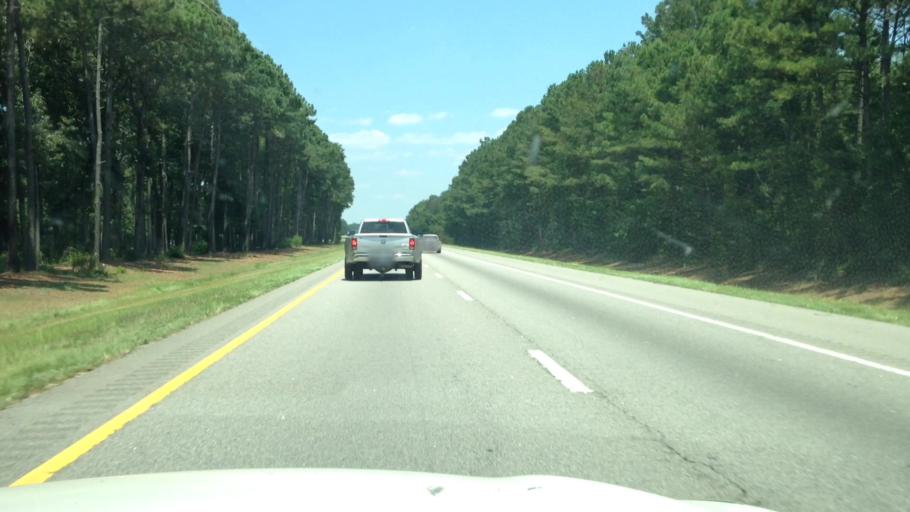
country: US
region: North Carolina
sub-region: Robeson County
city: Rowland
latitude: 34.5469
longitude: -79.2130
